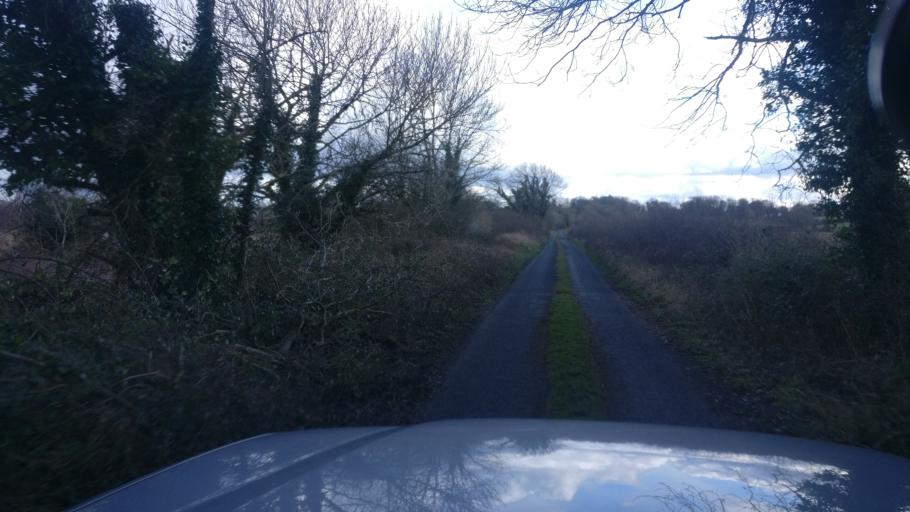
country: IE
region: Connaught
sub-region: County Galway
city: Loughrea
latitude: 53.1903
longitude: -8.4299
